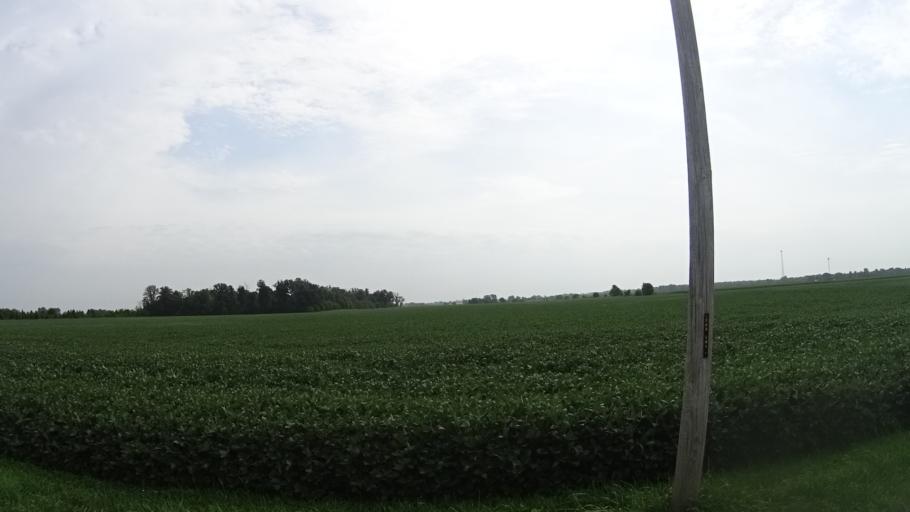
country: US
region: Indiana
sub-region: Madison County
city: Lapel
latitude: 40.0255
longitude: -85.8055
